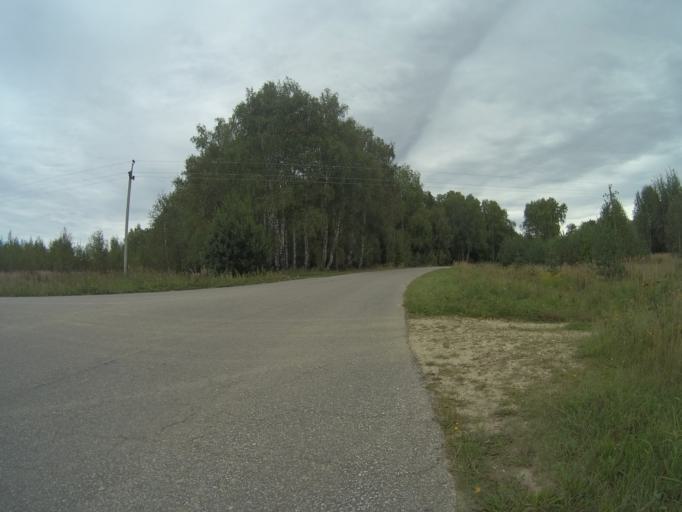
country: RU
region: Vladimir
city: Golovino
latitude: 55.9869
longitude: 40.5202
